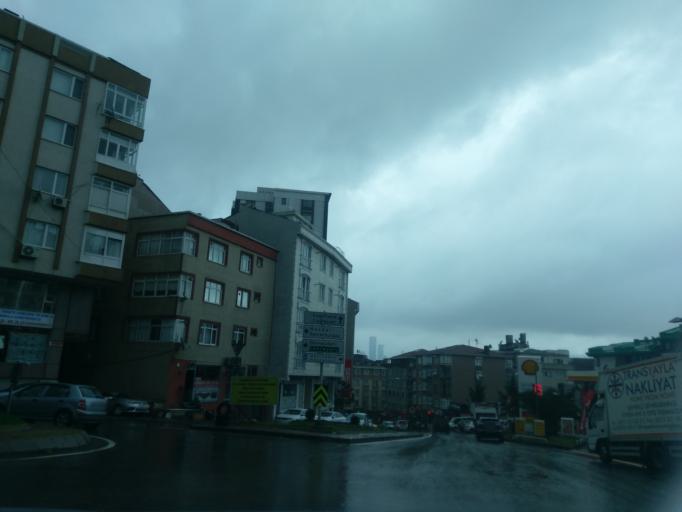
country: TR
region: Istanbul
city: Sisli
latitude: 41.0860
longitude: 28.9680
